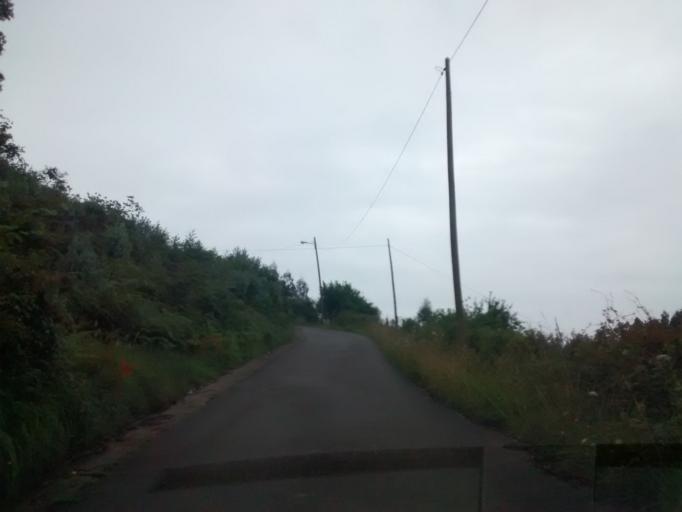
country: ES
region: Asturias
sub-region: Province of Asturias
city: Villaviciosa
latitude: 43.5412
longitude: -5.4081
